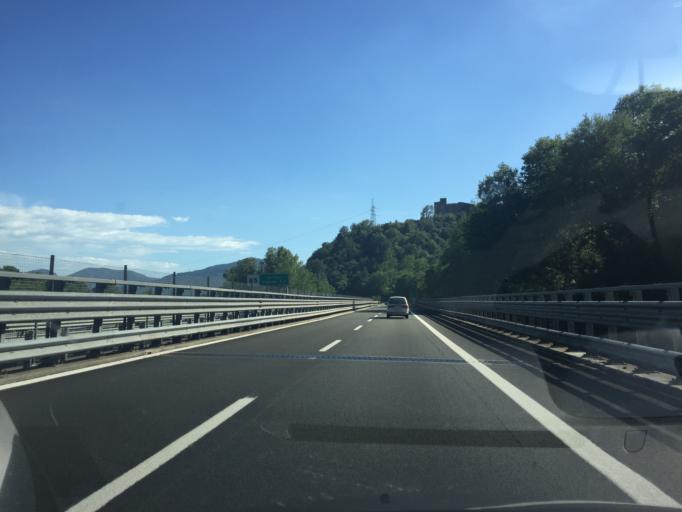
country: IT
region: Tuscany
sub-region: Provincia di Massa-Carrara
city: Villafranca in Lunigiana
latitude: 44.2710
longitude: 9.9517
